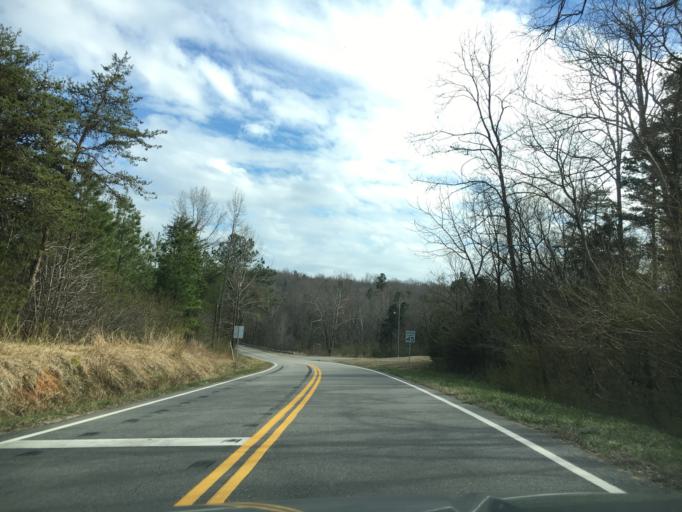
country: US
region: Virginia
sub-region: Halifax County
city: Halifax
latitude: 36.7649
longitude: -78.9160
